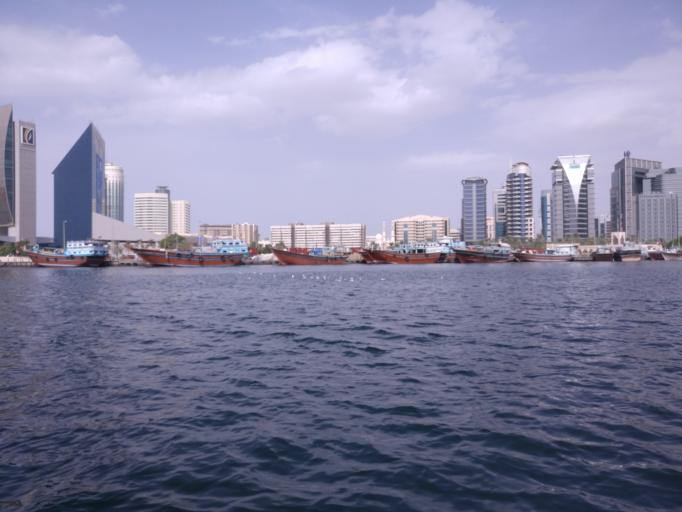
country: AE
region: Ash Shariqah
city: Sharjah
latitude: 25.2562
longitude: 55.3157
